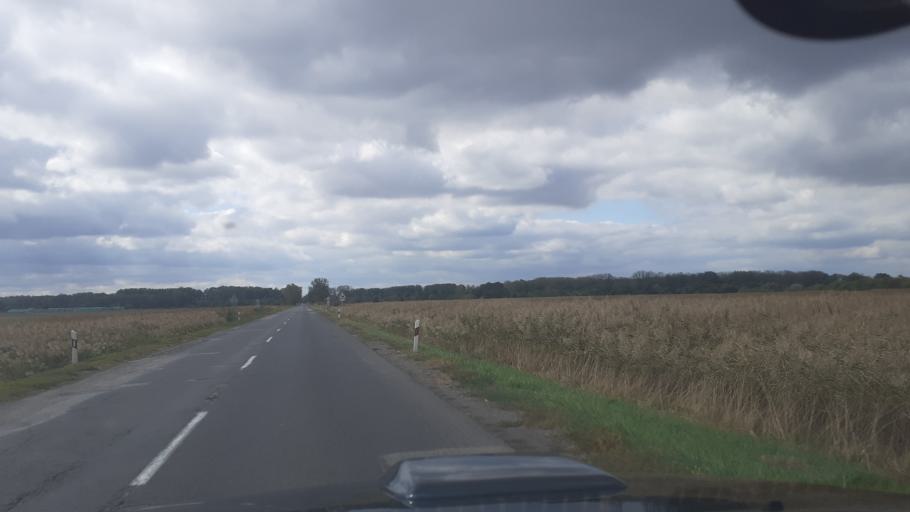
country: HU
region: Bacs-Kiskun
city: Fulopszallas
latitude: 46.8107
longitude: 19.1723
